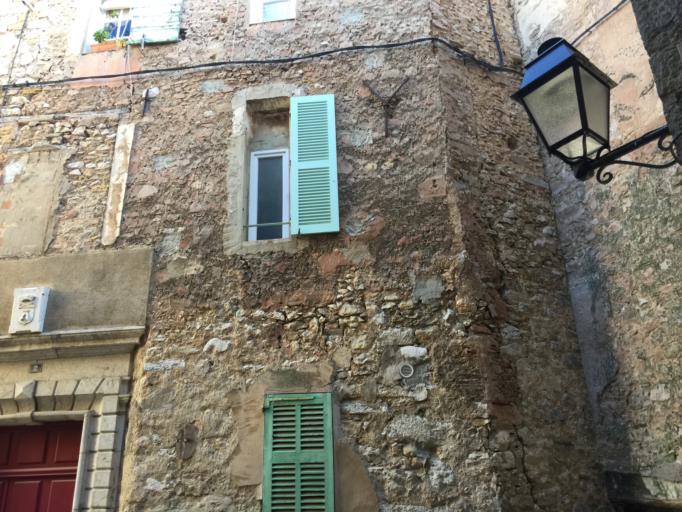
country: FR
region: Provence-Alpes-Cote d'Azur
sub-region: Departement du Var
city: Le Castellet
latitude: 43.1964
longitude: 5.7563
